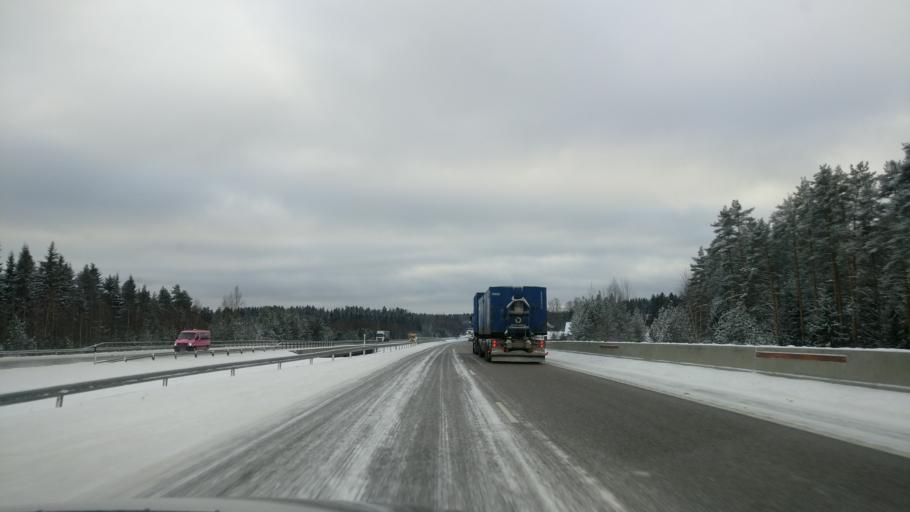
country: FI
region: Paijanne Tavastia
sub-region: Lahti
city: Nastola
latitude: 61.1025
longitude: 25.9109
